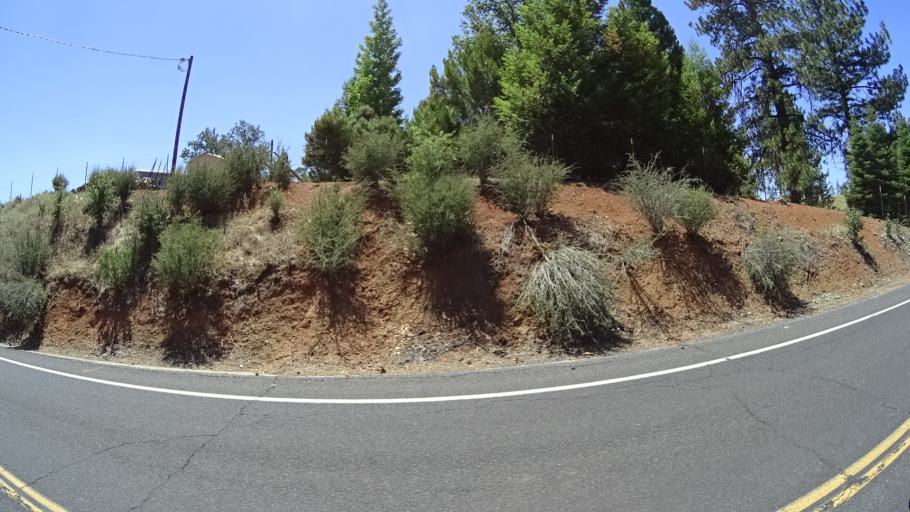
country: US
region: California
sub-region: Calaveras County
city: Mountain Ranch
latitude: 38.2694
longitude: -120.5046
